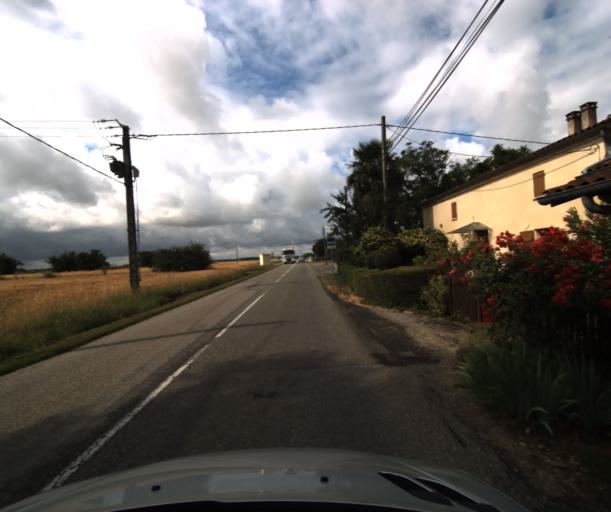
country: FR
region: Midi-Pyrenees
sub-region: Departement du Tarn-et-Garonne
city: Saint-Nicolas-de-la-Grave
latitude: 43.9998
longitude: 0.9873
